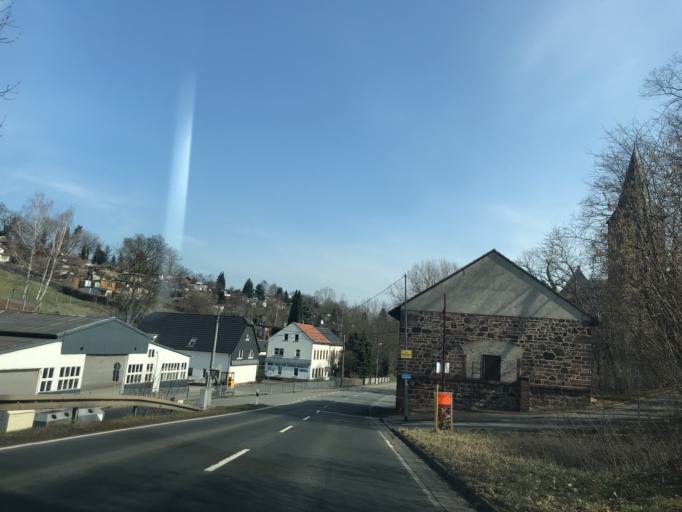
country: DE
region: Saxony
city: Rochlitz
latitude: 51.0445
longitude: 12.7886
